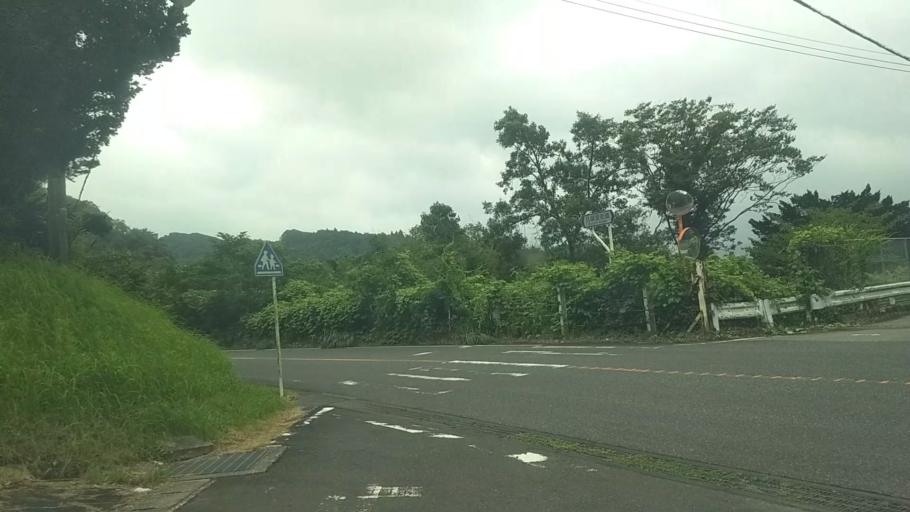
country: JP
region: Chiba
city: Kawaguchi
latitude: 35.2512
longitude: 140.0734
